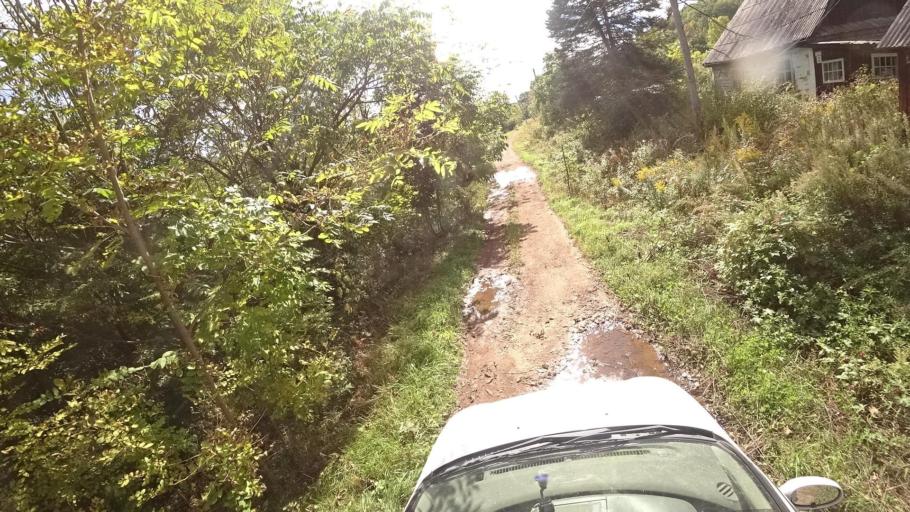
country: RU
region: Primorskiy
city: Yakovlevka
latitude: 44.3918
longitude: 133.6038
